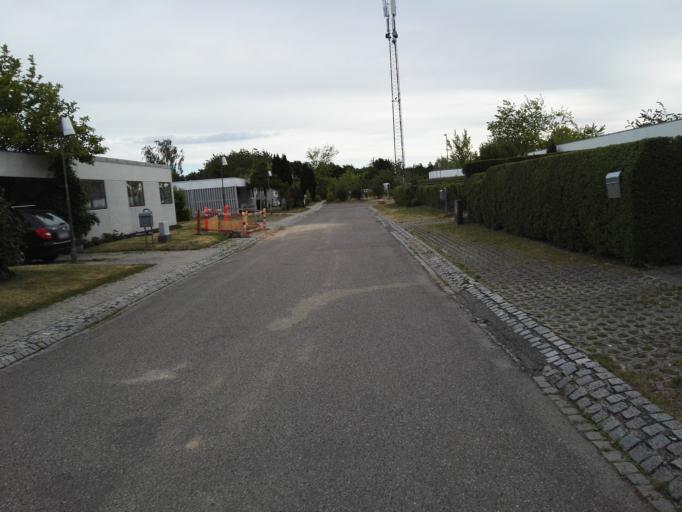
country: DK
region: Capital Region
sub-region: Ballerup Kommune
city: Ballerup
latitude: 55.7470
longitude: 12.3702
